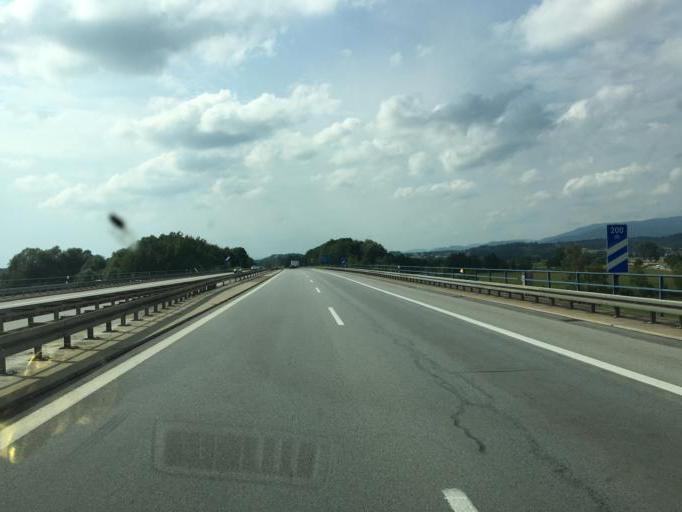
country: DE
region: Bavaria
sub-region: Lower Bavaria
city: Metten
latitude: 48.8440
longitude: 12.8933
